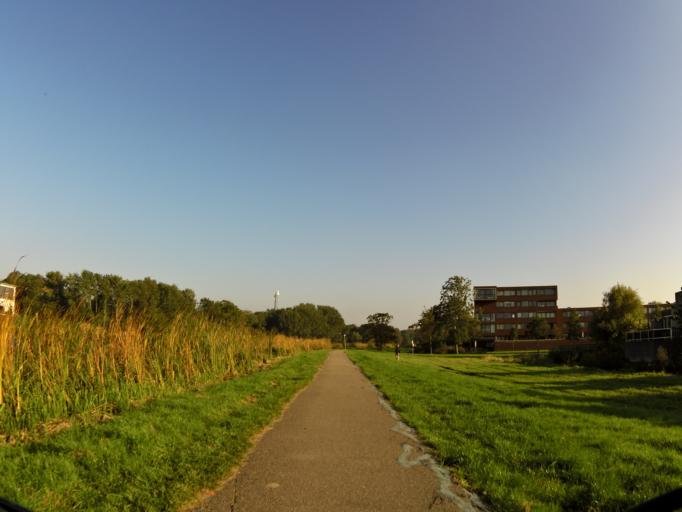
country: NL
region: South Holland
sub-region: Gemeente Leiderdorp
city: Leiderdorp
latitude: 52.1692
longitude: 4.5347
